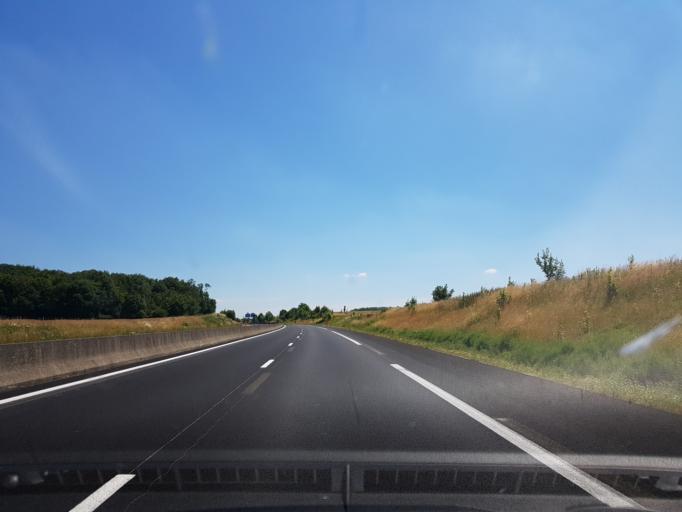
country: FR
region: Picardie
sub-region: Departement de l'Aisne
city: Holnon
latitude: 49.8431
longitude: 3.2085
